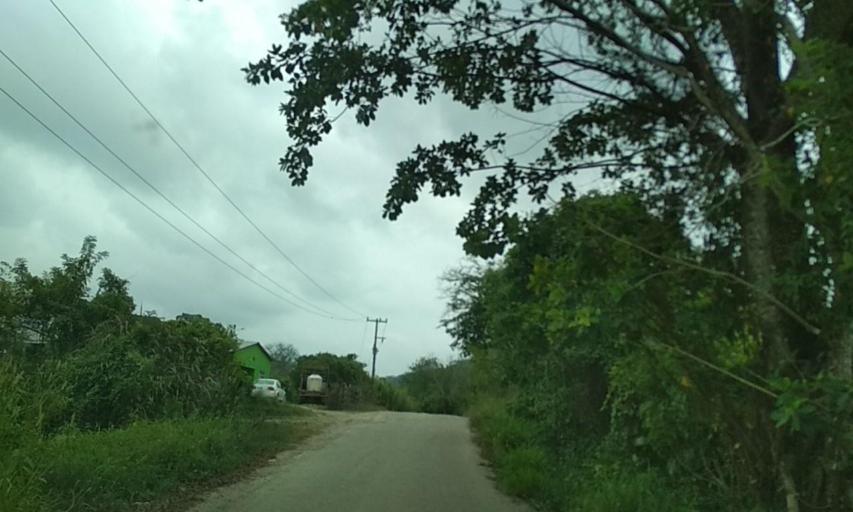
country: MX
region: Veracruz
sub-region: Uxpanapa
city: Poblado 10
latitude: 17.4948
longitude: -94.1317
